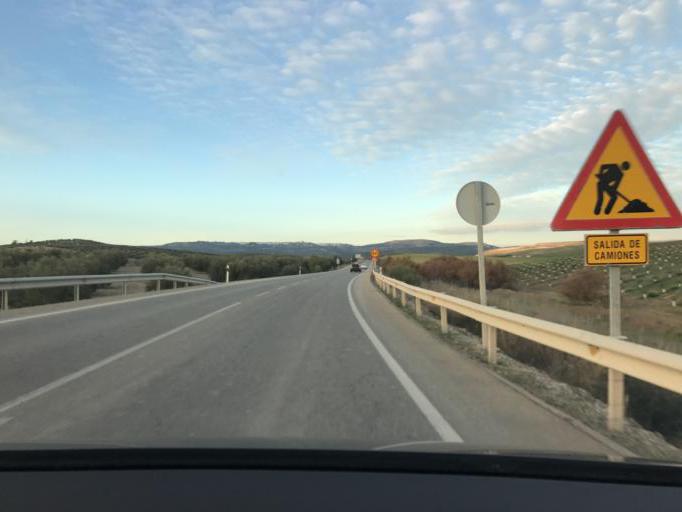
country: ES
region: Andalusia
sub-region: Provincia de Jaen
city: Ubeda
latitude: 37.9440
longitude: -3.3597
